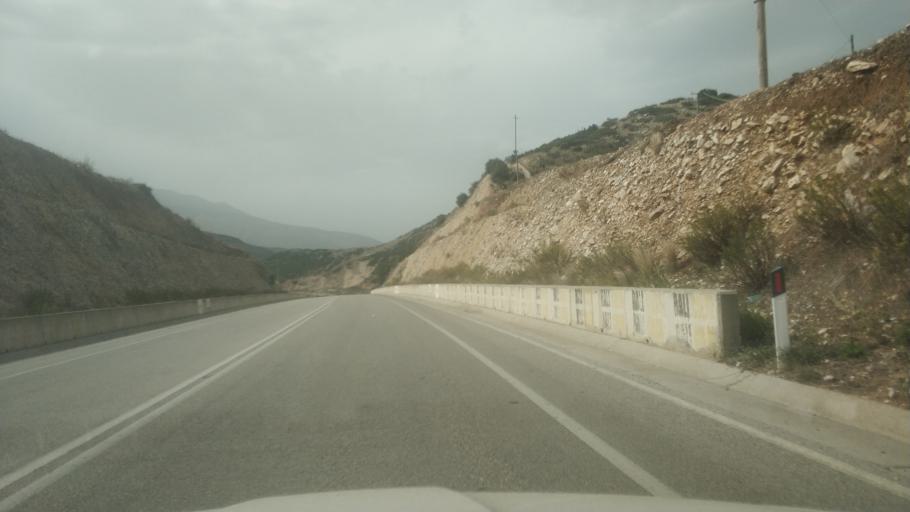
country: AL
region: Gjirokaster
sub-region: Rrethi i Tepelenes
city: Memaliaj
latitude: 40.3641
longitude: 19.9228
